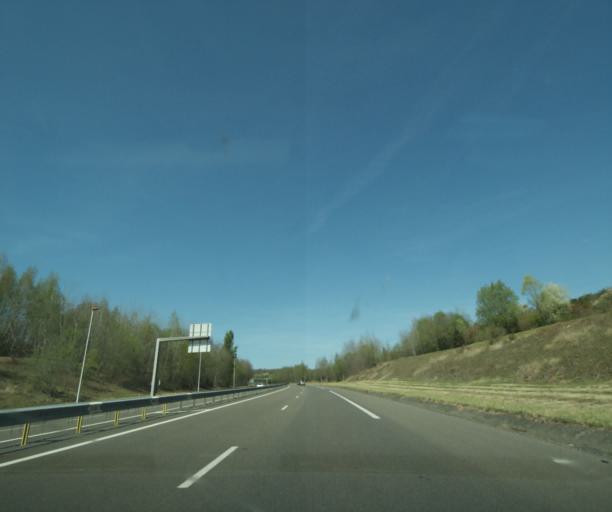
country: FR
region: Bourgogne
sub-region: Departement de la Nievre
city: Coulanges-les-Nevers
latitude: 47.0161
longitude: 3.1990
